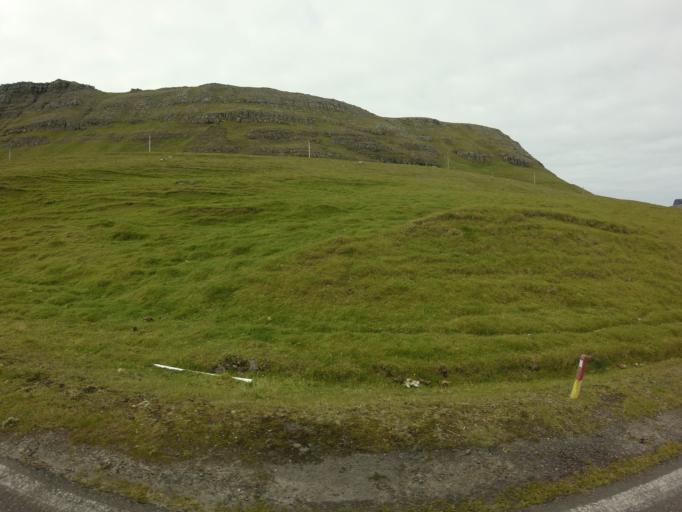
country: FO
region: Suduroy
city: Tvoroyri
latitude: 61.5909
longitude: -6.9470
